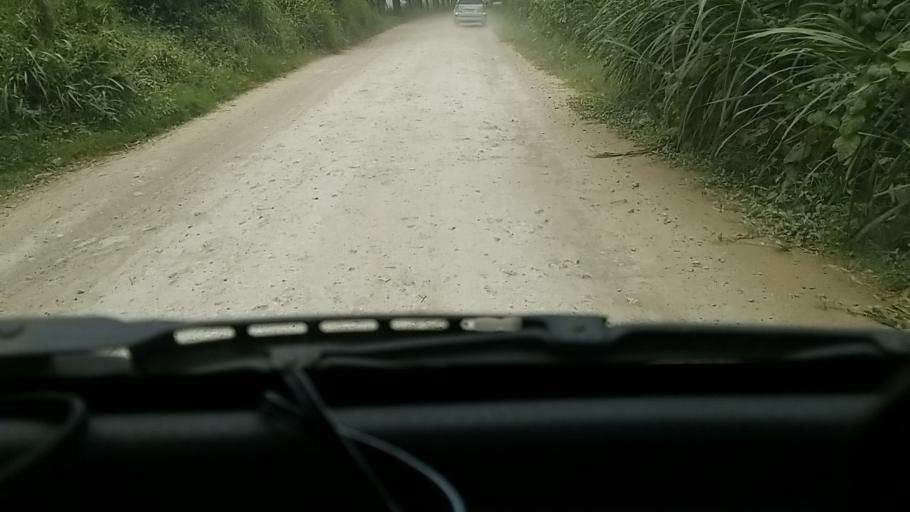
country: CD
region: Nord Kivu
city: Sake
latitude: -1.5958
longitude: 29.0399
